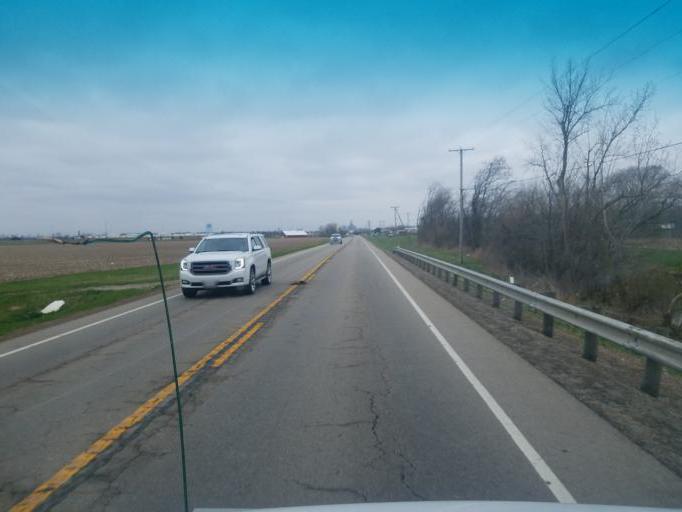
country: US
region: Ohio
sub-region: Van Wert County
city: Van Wert
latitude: 40.8957
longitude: -84.5783
